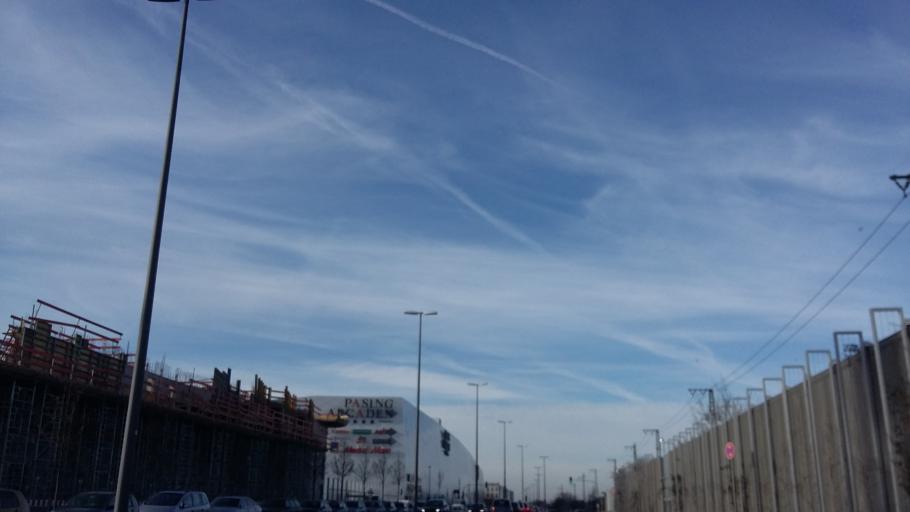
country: DE
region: Bavaria
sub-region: Upper Bavaria
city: Pasing
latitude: 48.1477
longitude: 11.4675
